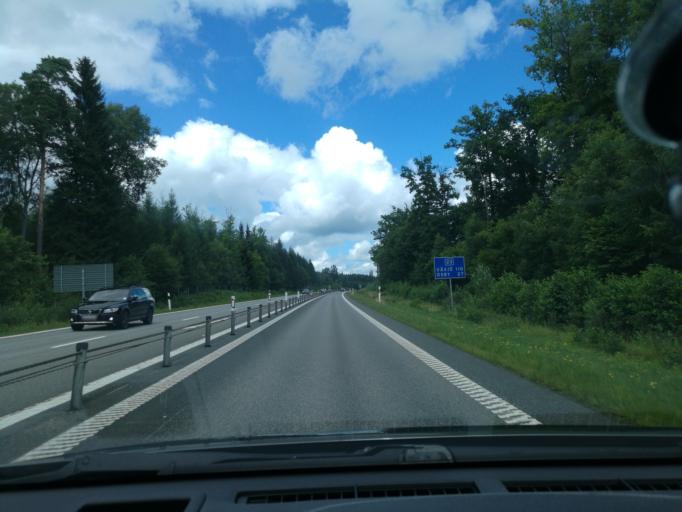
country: SE
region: Skane
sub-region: Hassleholms Kommun
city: Hassleholm
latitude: 56.1860
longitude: 13.8453
